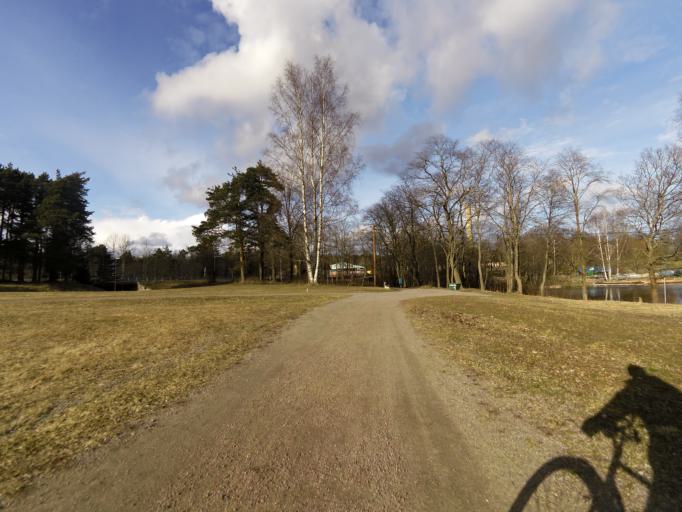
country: SE
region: Gaevleborg
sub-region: Gavle Kommun
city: Gavle
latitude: 60.6735
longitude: 17.1091
